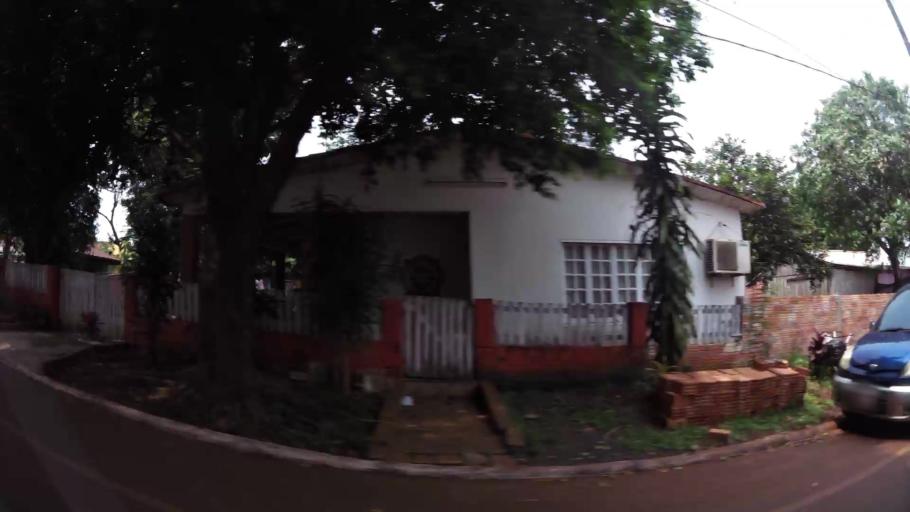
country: PY
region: Alto Parana
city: Presidente Franco
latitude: -25.5564
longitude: -54.6278
